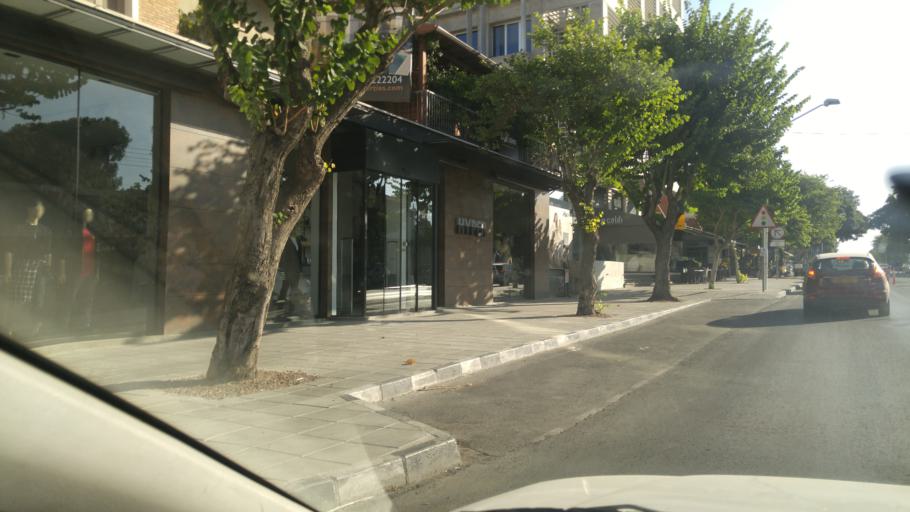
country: CY
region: Limassol
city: Limassol
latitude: 34.6863
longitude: 33.0345
